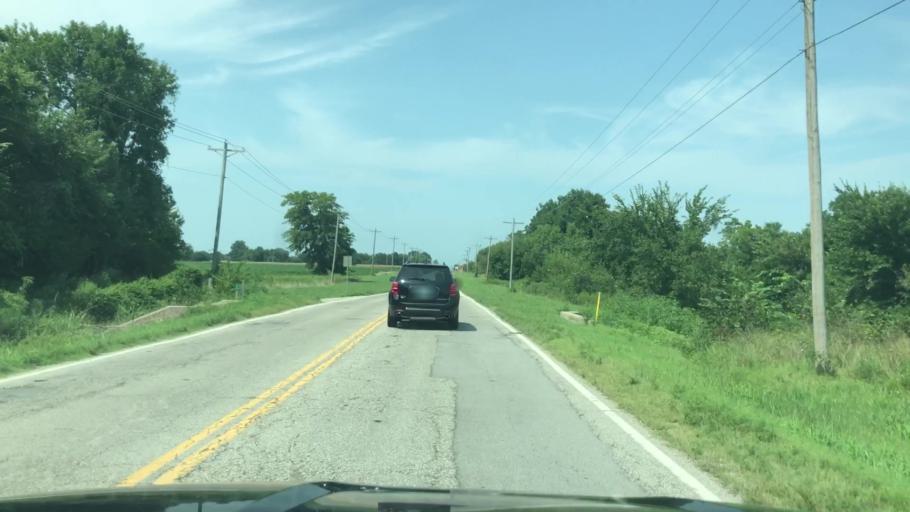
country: US
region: Oklahoma
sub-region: Ottawa County
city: Miami
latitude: 36.8960
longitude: -94.8418
